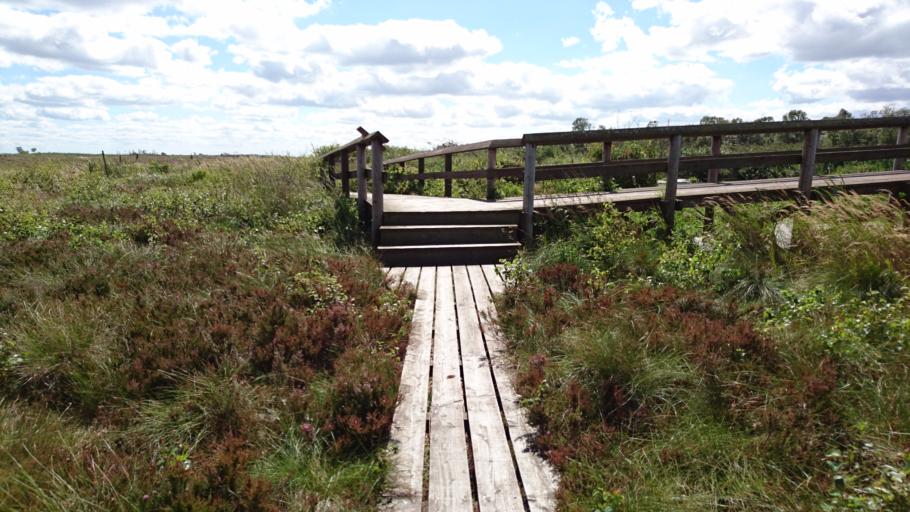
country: DK
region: North Denmark
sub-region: Alborg Kommune
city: Storvorde
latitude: 56.9108
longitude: 10.1825
